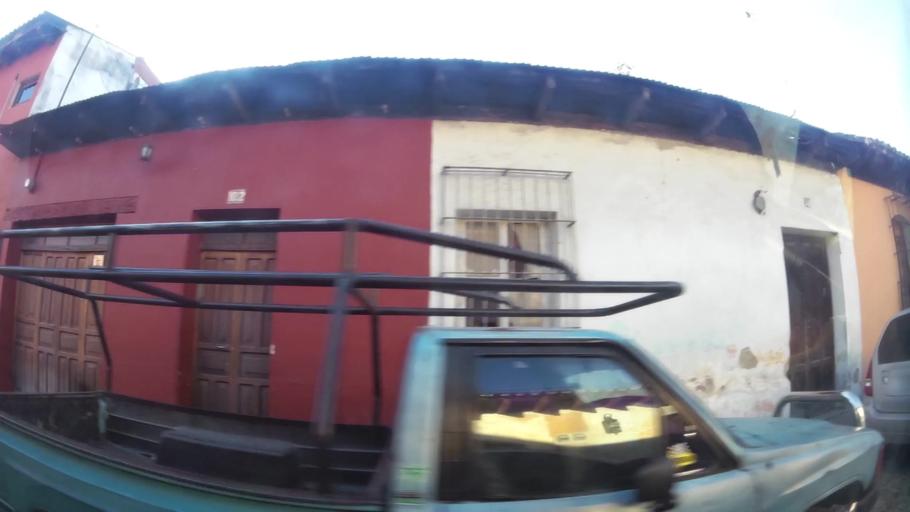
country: GT
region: Sacatepequez
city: Antigua Guatemala
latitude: 14.5630
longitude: -90.7364
